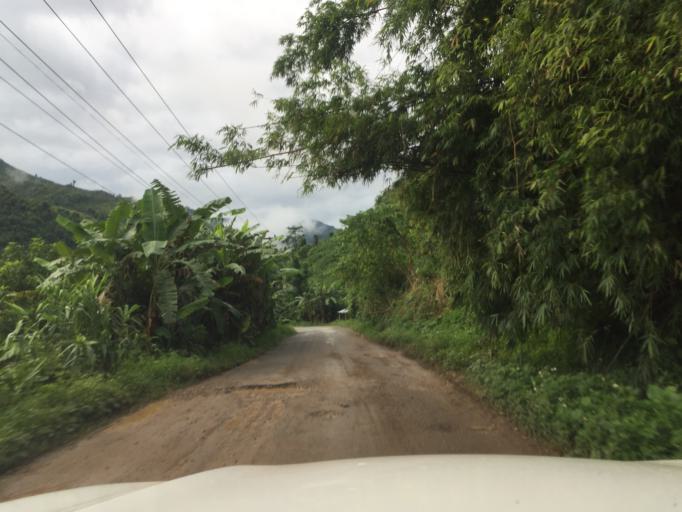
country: LA
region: Oudomxai
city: Muang La
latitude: 21.0627
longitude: 102.2401
